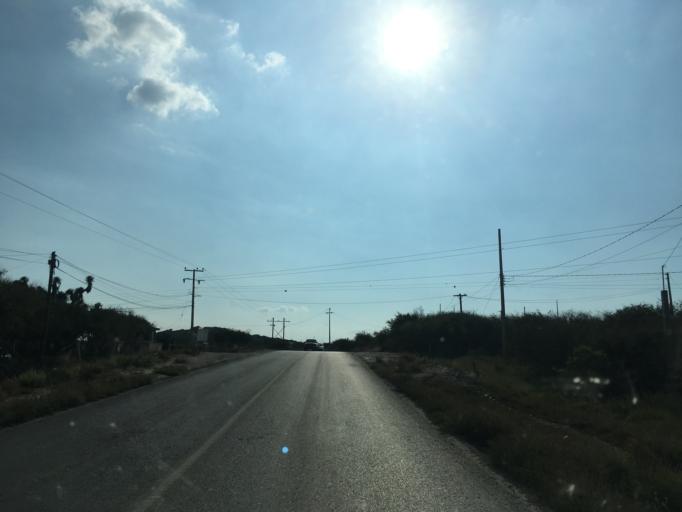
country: MX
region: Hidalgo
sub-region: Ixmiquilpan
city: El Nith
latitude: 20.5751
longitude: -99.1401
